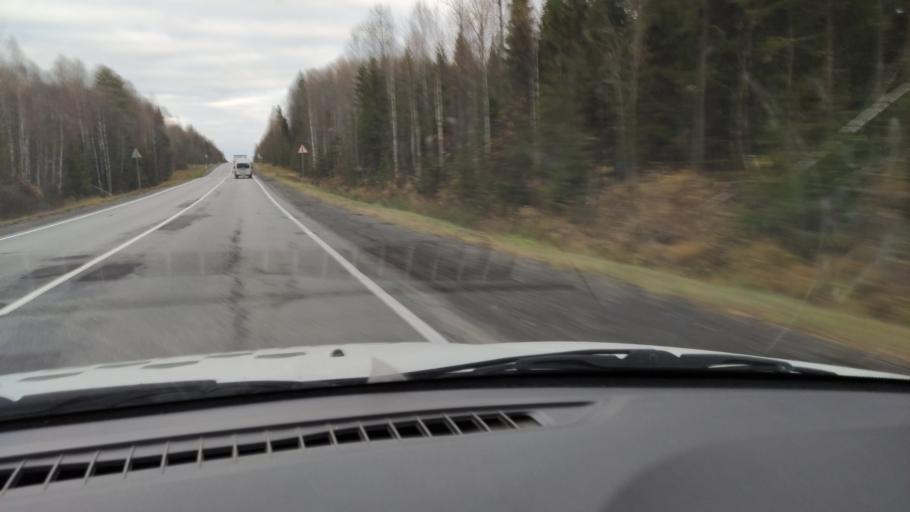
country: RU
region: Kirov
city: Chernaya Kholunitsa
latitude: 58.8587
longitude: 51.6330
